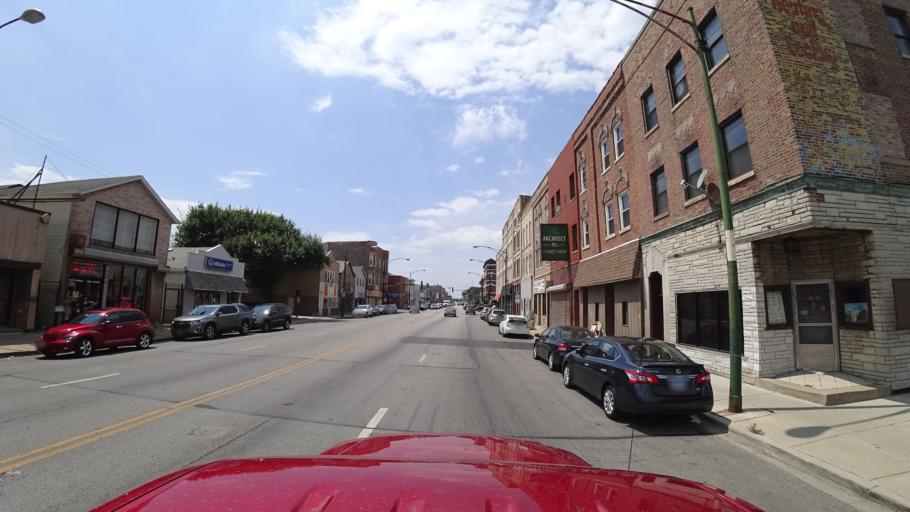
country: US
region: Illinois
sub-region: Cook County
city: Chicago
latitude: 41.8422
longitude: -87.6568
